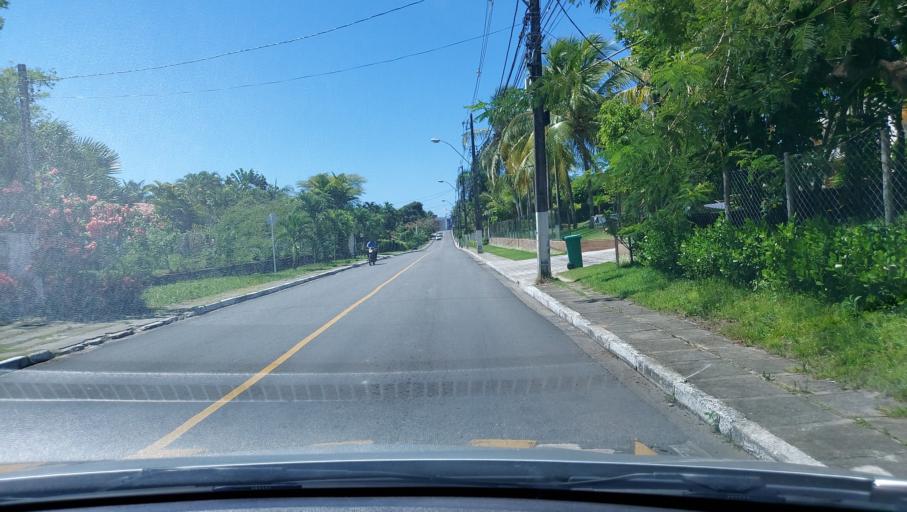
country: BR
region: Bahia
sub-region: Lauro De Freitas
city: Lauro de Freitas
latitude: -12.8700
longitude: -38.3064
